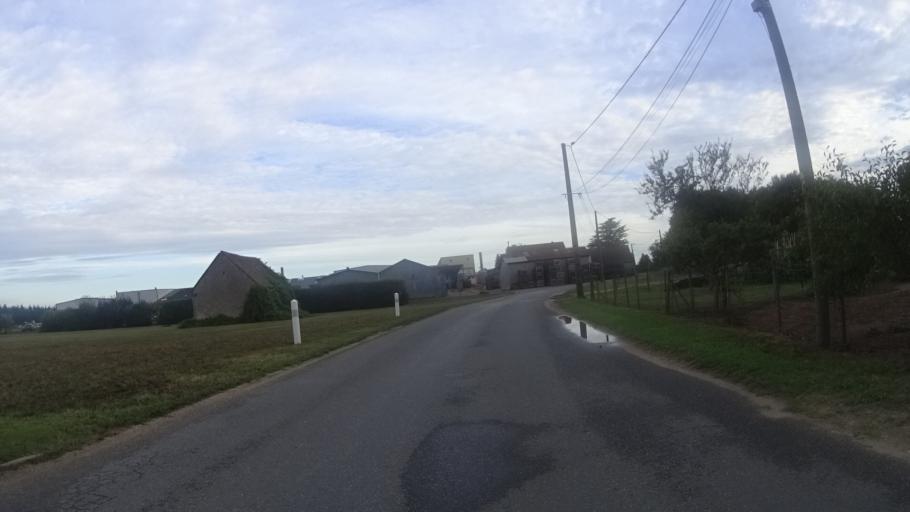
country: FR
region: Centre
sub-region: Departement du Loiret
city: Saint-Benoit-sur-Loire
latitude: 47.7924
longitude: 2.3136
